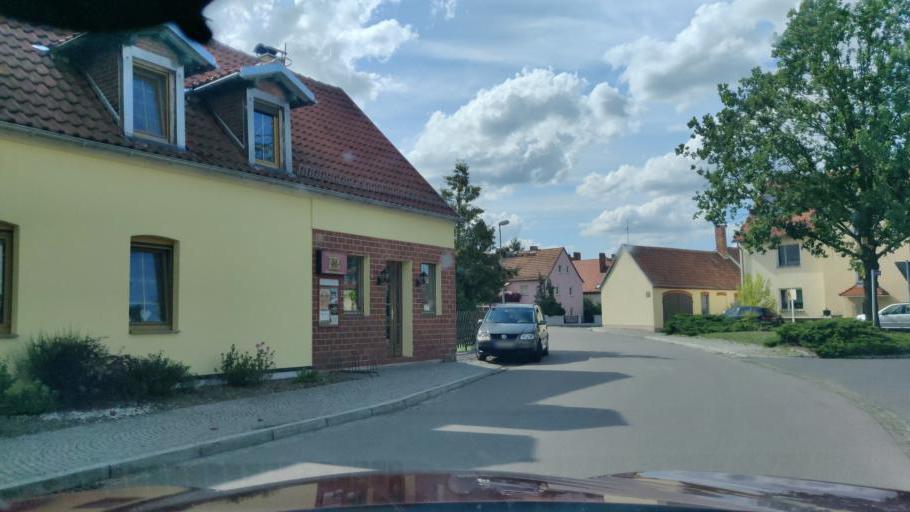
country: DE
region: Saxony
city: Schildau
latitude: 51.4906
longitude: 12.9026
